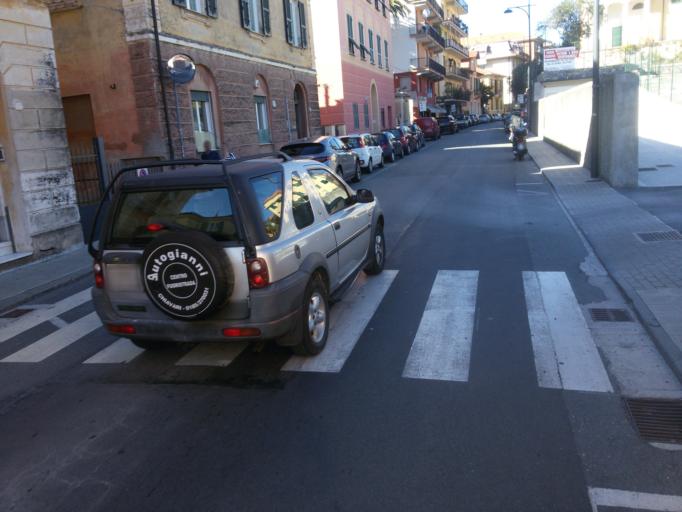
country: IT
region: Liguria
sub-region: Provincia di Genova
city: Chiavari
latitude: 44.3226
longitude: 9.3227
